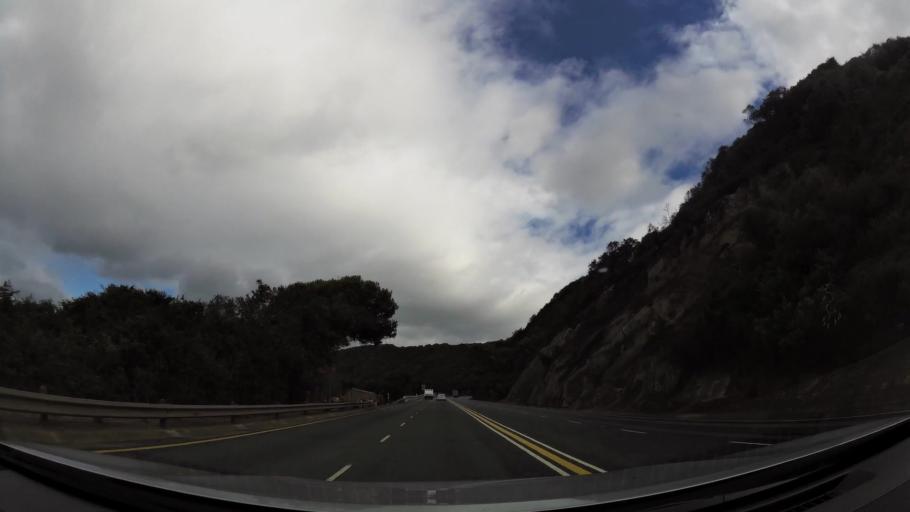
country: ZA
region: Western Cape
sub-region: Eden District Municipality
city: George
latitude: -33.9948
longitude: 22.5666
